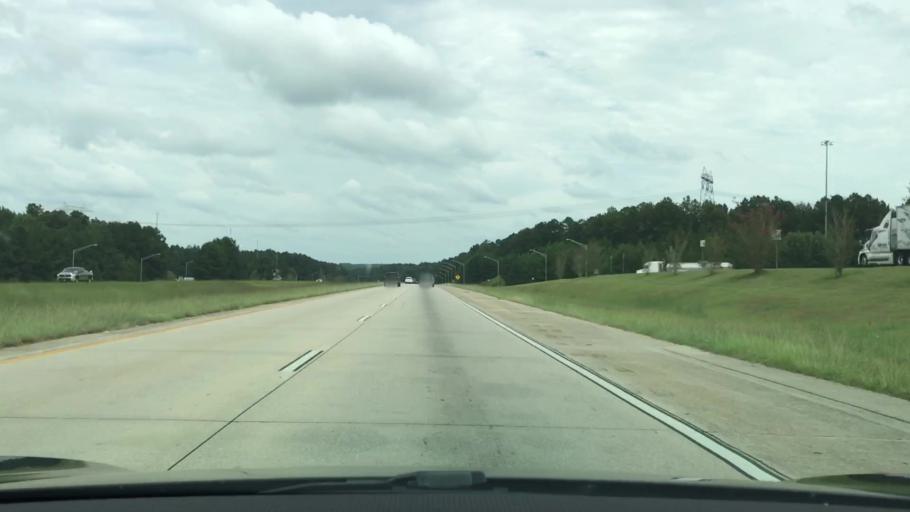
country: US
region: Georgia
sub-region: Troup County
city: Hogansville
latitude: 33.0839
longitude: -84.9172
